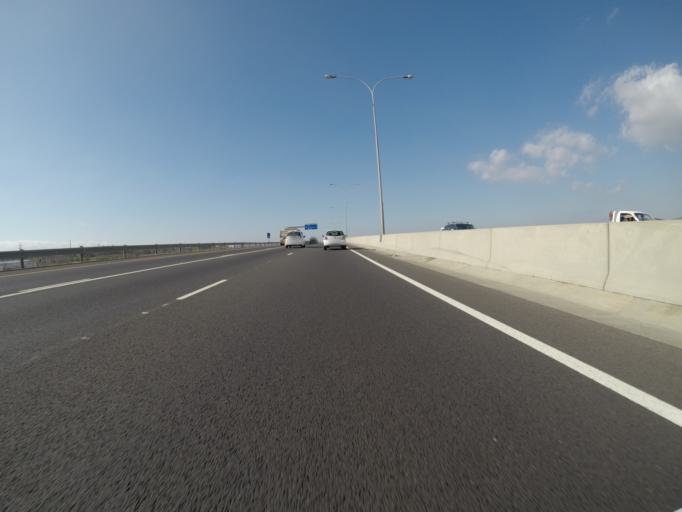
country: ZA
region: Western Cape
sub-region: City of Cape Town
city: Kraaifontein
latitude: -33.9205
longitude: 18.6648
